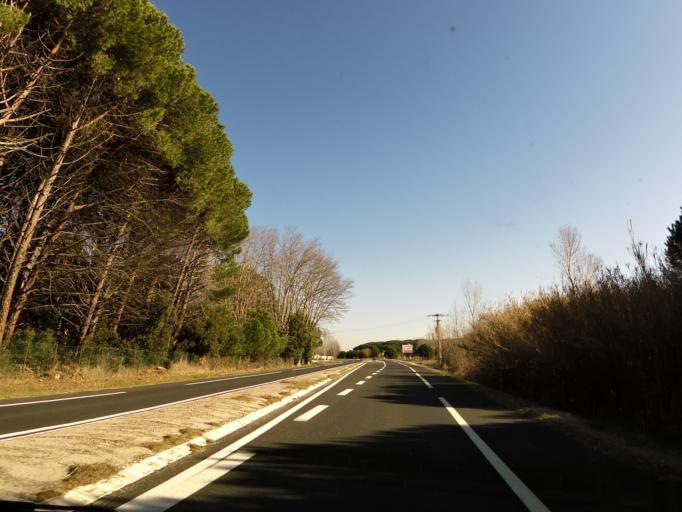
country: FR
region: Languedoc-Roussillon
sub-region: Departement du Gard
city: Aigues-Mortes
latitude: 43.5842
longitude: 4.2330
